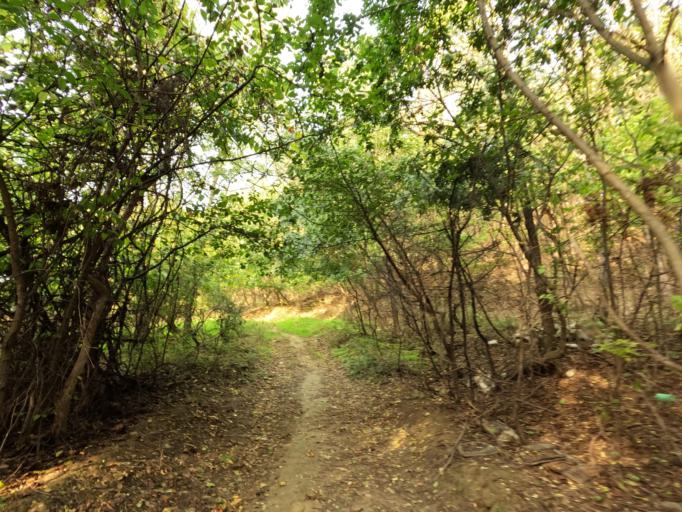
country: HU
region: Tolna
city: Szekszard
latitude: 46.3409
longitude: 18.6726
